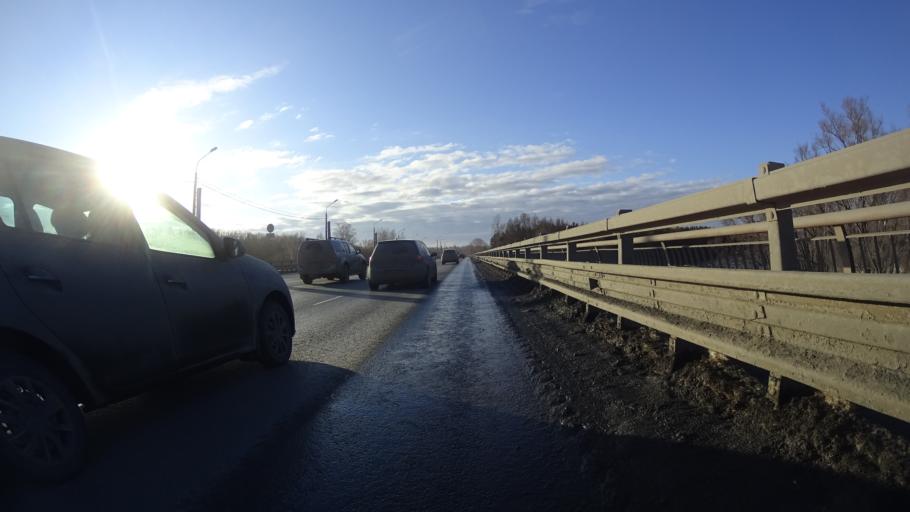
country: RU
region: Chelyabinsk
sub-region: Gorod Chelyabinsk
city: Chelyabinsk
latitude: 55.1482
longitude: 61.3257
